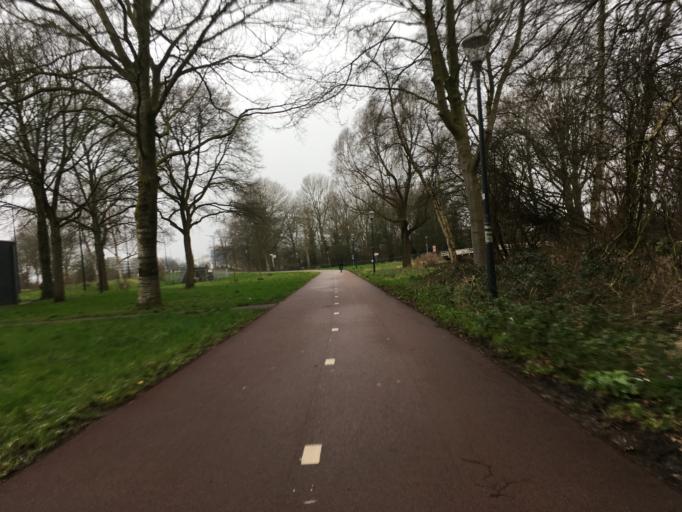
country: NL
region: North Holland
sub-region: Gemeente Heemstede
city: Heemstede
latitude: 52.3553
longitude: 4.6427
